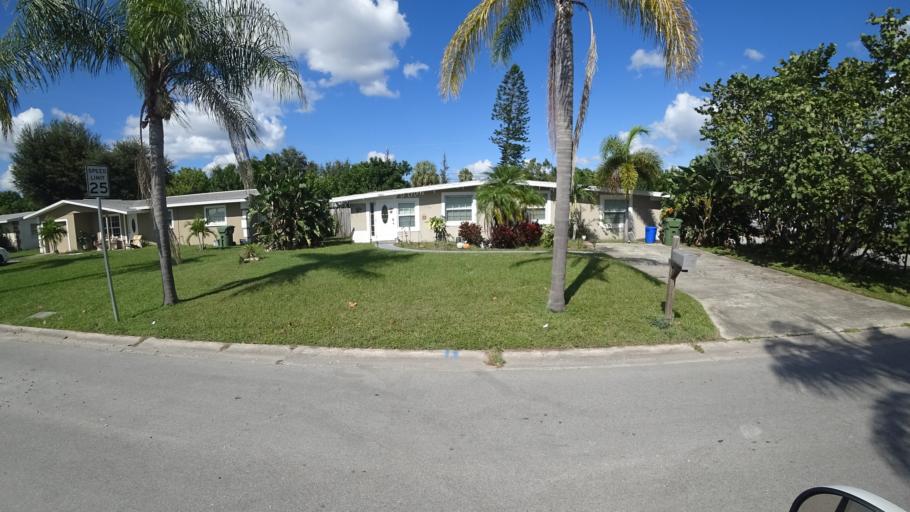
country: US
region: Florida
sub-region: Manatee County
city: South Bradenton
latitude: 27.4777
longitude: -82.5814
